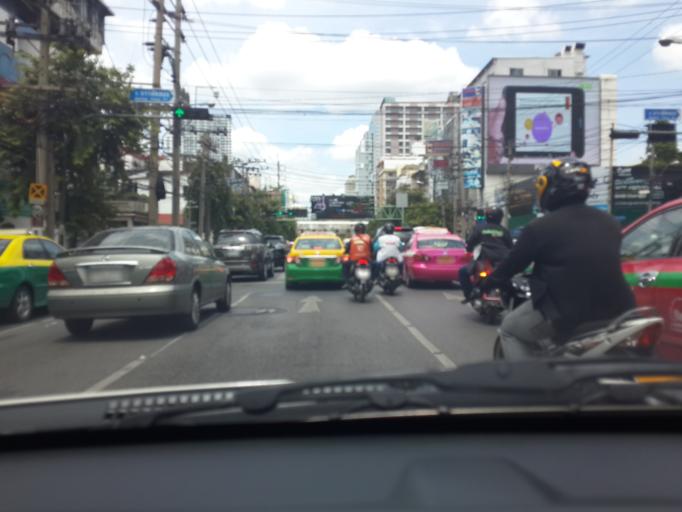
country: TH
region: Bangkok
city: Ratchathewi
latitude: 13.7551
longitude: 100.5266
